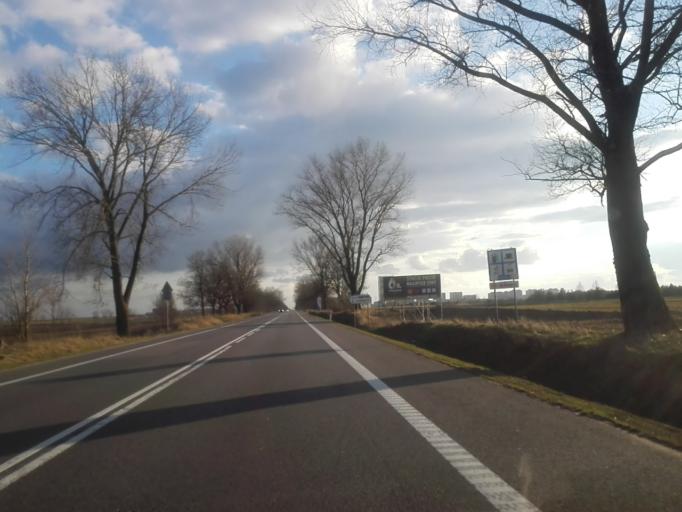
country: PL
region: Podlasie
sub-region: Suwalki
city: Suwalki
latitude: 54.1355
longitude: 22.9552
